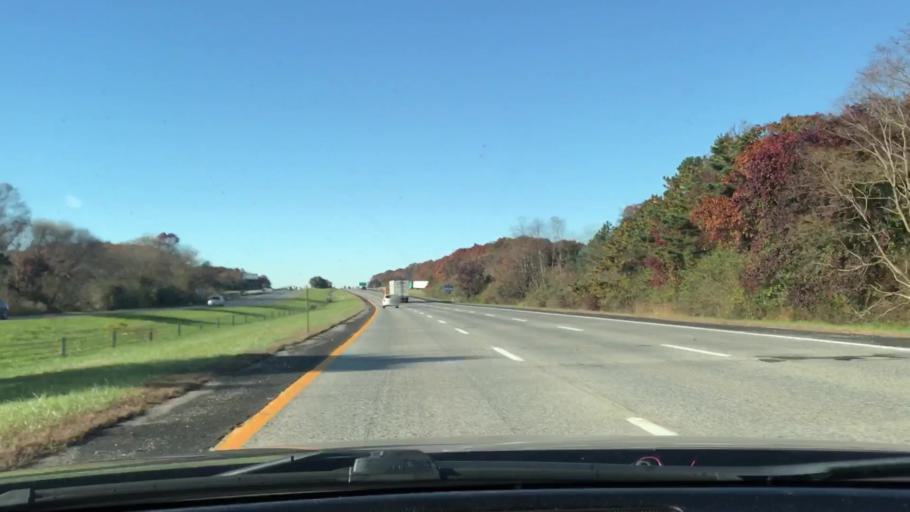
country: US
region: New York
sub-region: Suffolk County
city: Yaphank
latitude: 40.8462
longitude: -72.8839
